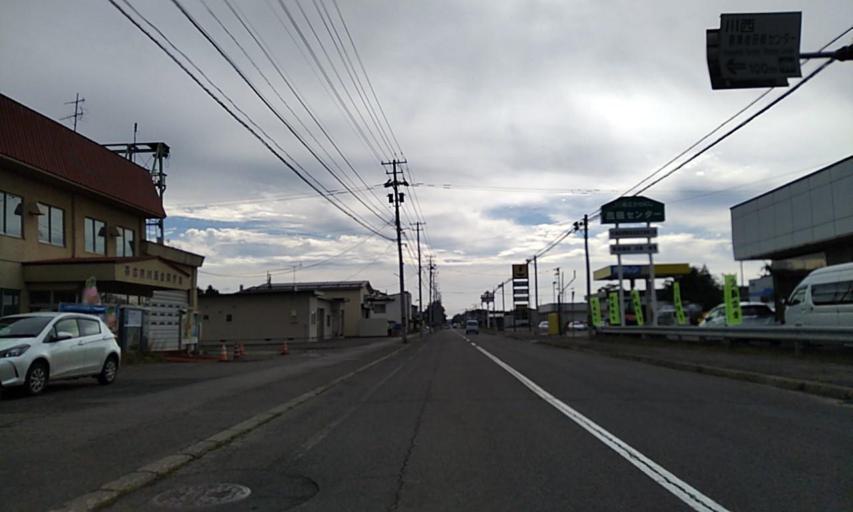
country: JP
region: Hokkaido
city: Obihiro
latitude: 42.8500
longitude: 143.1644
